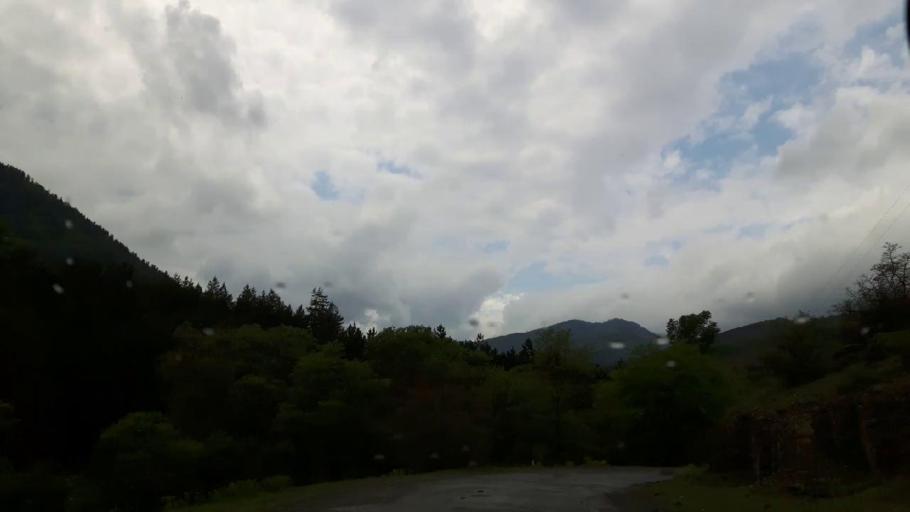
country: GE
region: Shida Kartli
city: Gori
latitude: 41.8956
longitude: 44.0298
